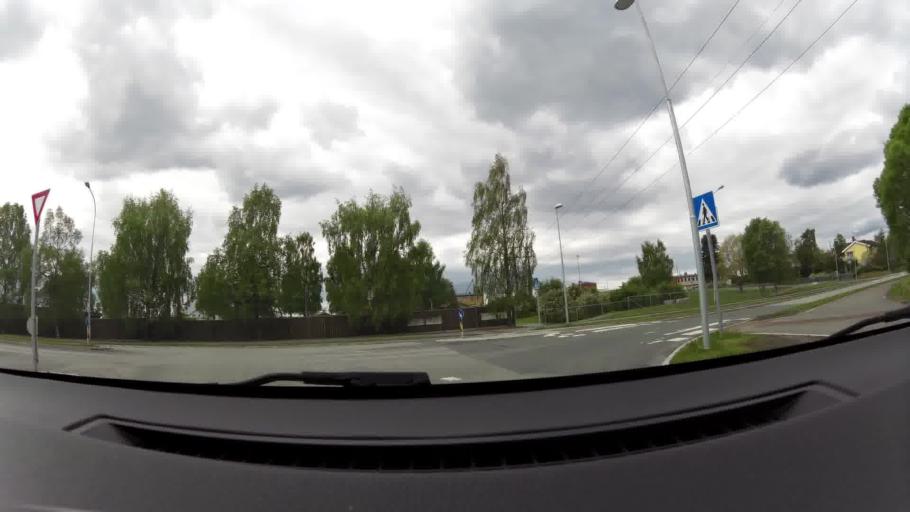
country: NO
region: Sor-Trondelag
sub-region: Trondheim
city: Trondheim
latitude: 63.3906
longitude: 10.4281
